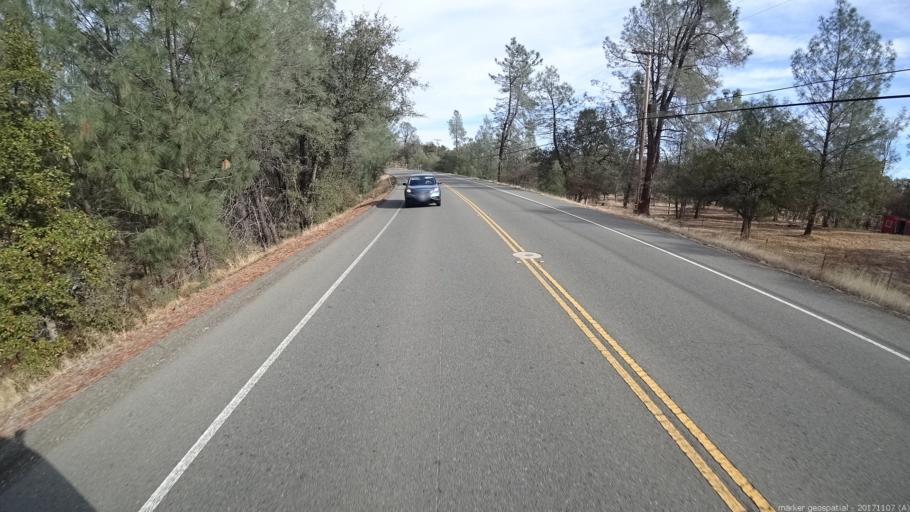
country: US
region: California
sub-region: Shasta County
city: Shasta
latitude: 40.5231
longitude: -122.4768
